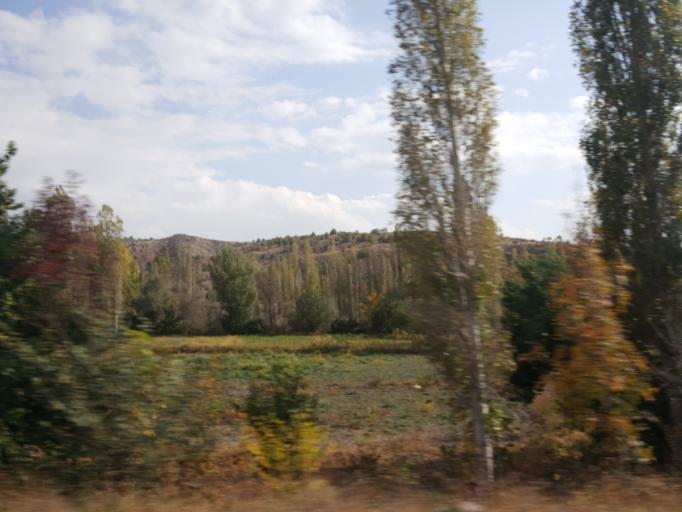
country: TR
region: Corum
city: Sungurlu
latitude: 40.1906
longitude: 34.5012
